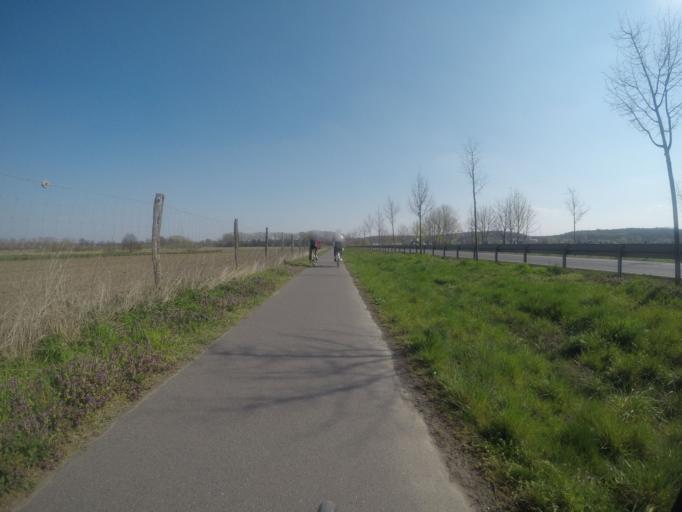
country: DE
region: Brandenburg
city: Potsdam
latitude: 52.4323
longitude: 12.9953
